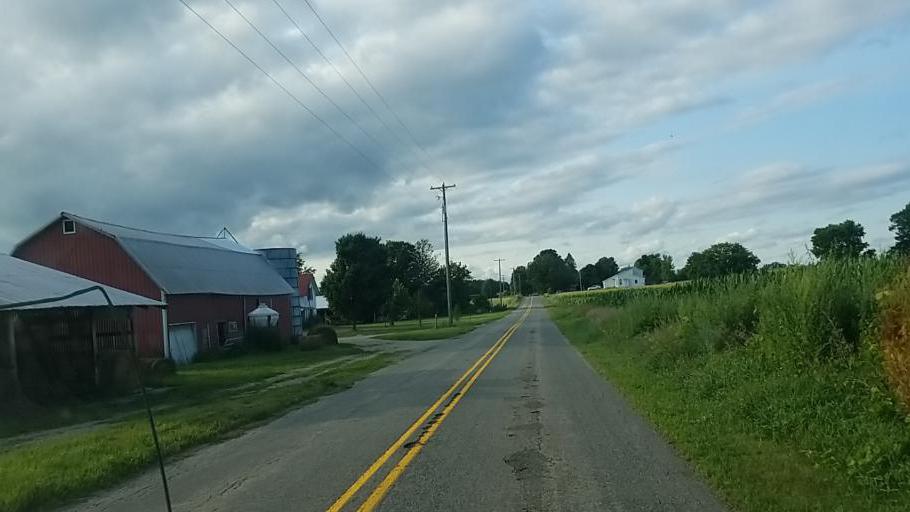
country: US
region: Michigan
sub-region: Montcalm County
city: Howard City
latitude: 43.2848
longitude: -85.3624
